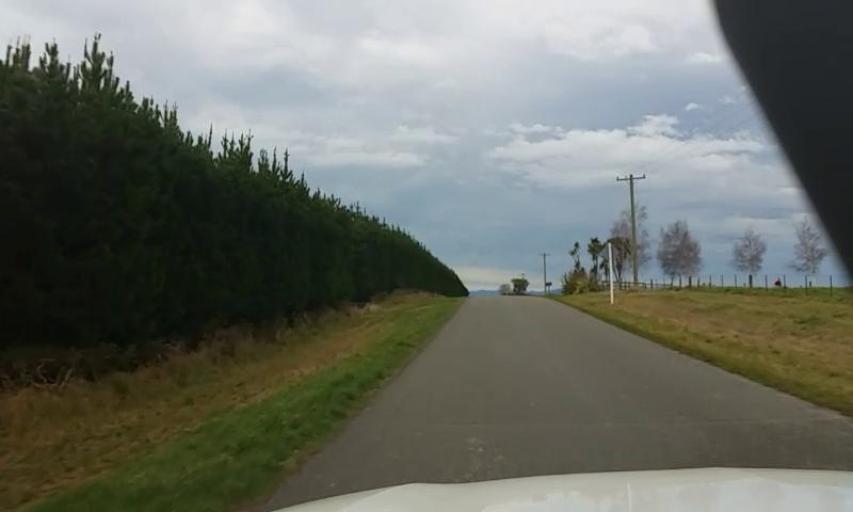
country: NZ
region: Canterbury
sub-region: Waimakariri District
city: Kaiapoi
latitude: -43.2924
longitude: 172.4716
